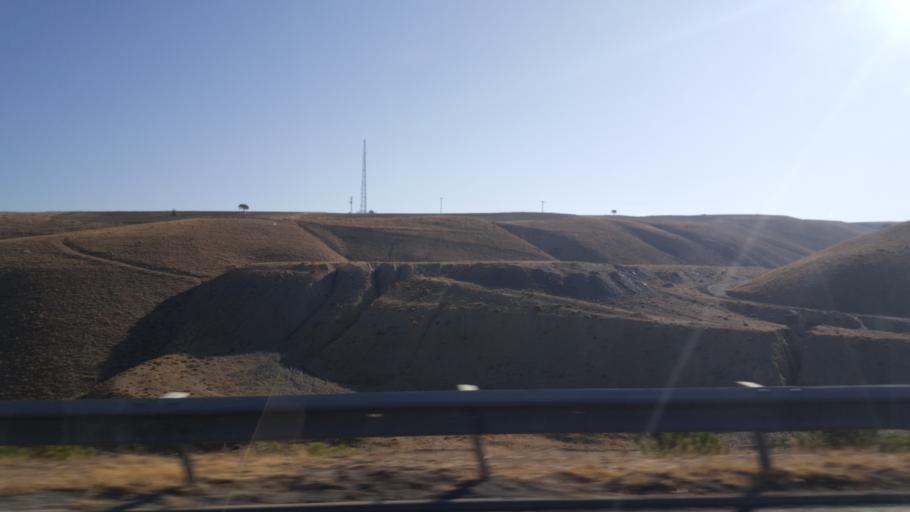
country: TR
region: Ankara
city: Cankaya
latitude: 39.8451
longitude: 32.8925
